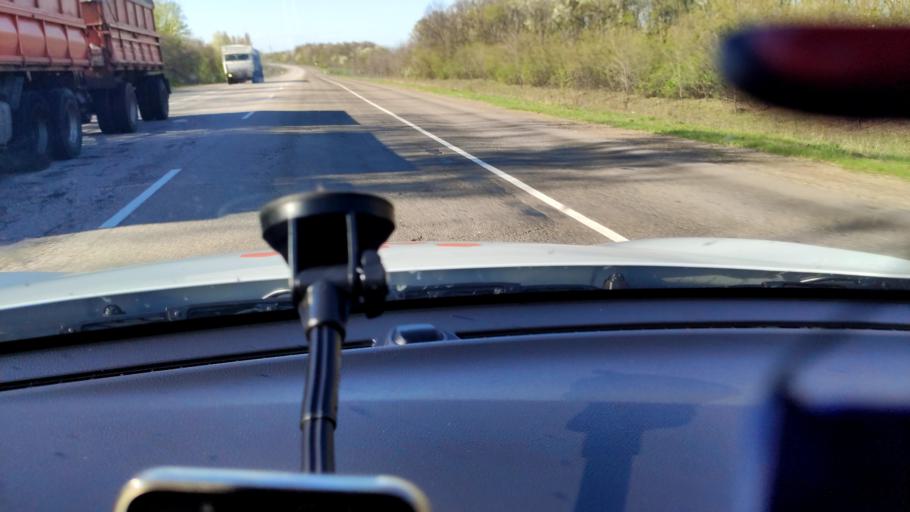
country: RU
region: Voronezj
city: Kolodeznyy
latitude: 51.2621
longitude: 39.0516
